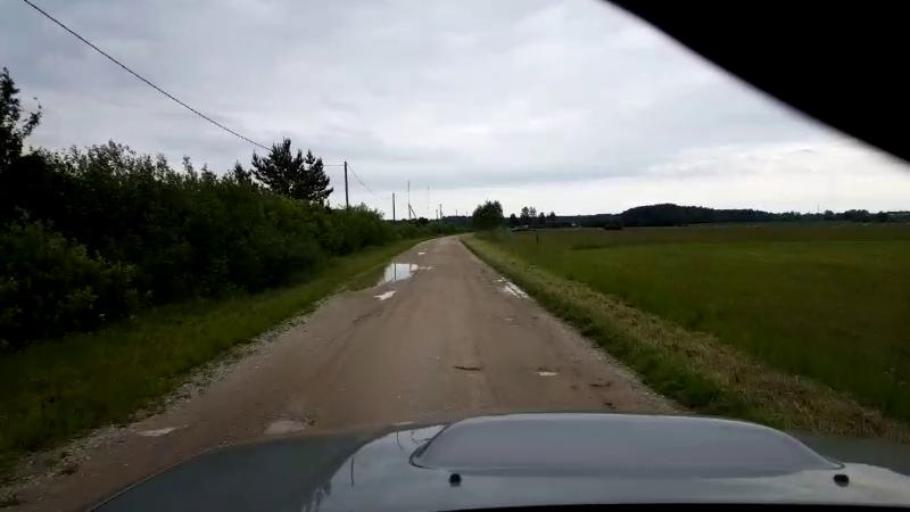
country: EE
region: Paernumaa
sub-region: Halinga vald
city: Parnu-Jaagupi
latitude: 58.5396
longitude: 24.5763
